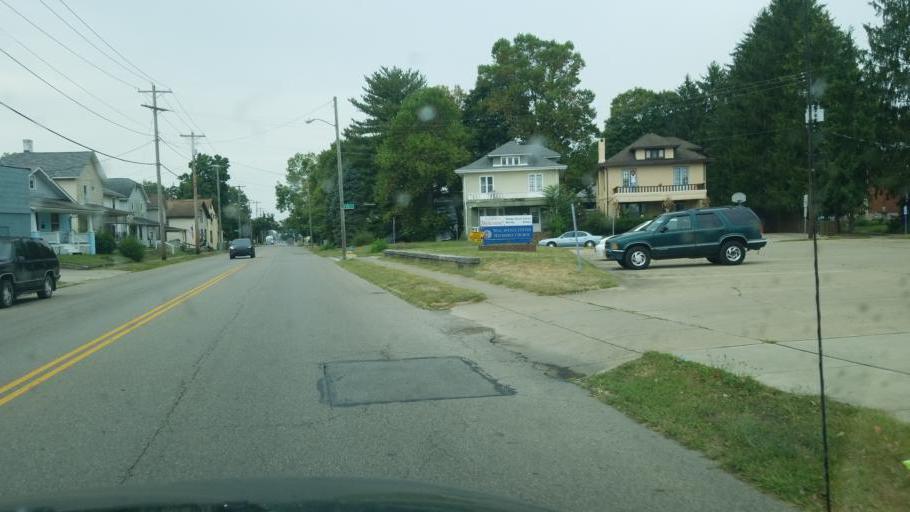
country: US
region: Ohio
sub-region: Licking County
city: Newark
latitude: 40.0521
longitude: -82.4273
